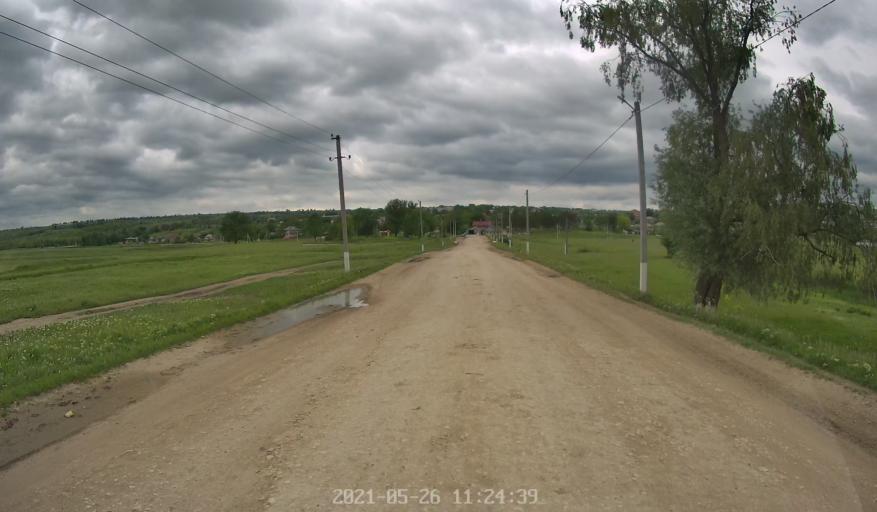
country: MD
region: Hincesti
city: Dancu
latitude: 46.8245
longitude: 28.3732
